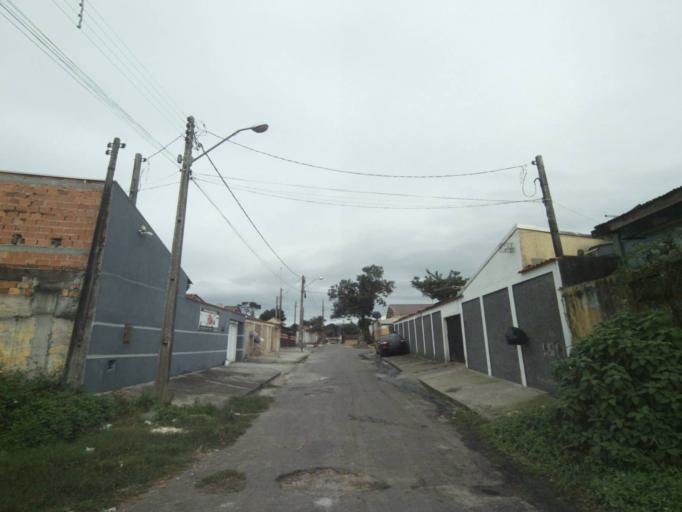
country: BR
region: Parana
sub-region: Paranagua
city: Paranagua
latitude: -25.5175
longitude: -48.5298
